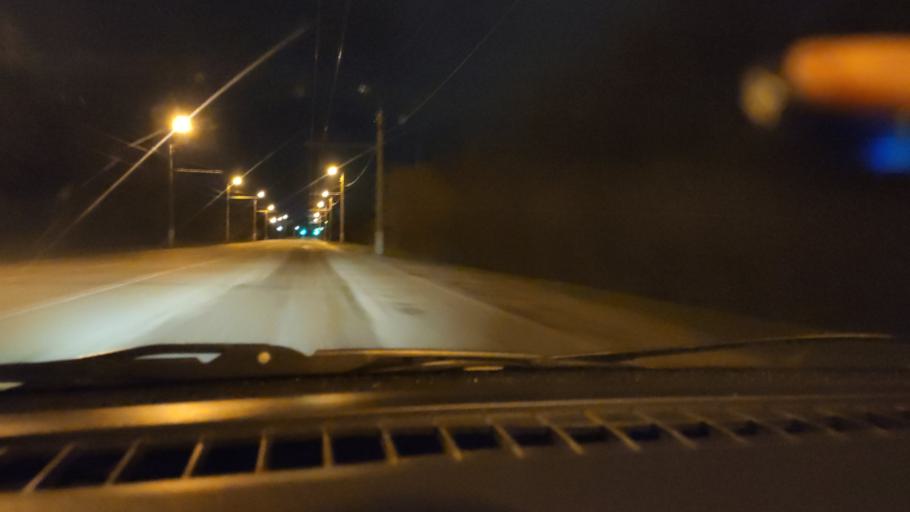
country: RU
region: Bashkortostan
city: Sterlitamak
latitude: 53.6595
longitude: 55.9238
